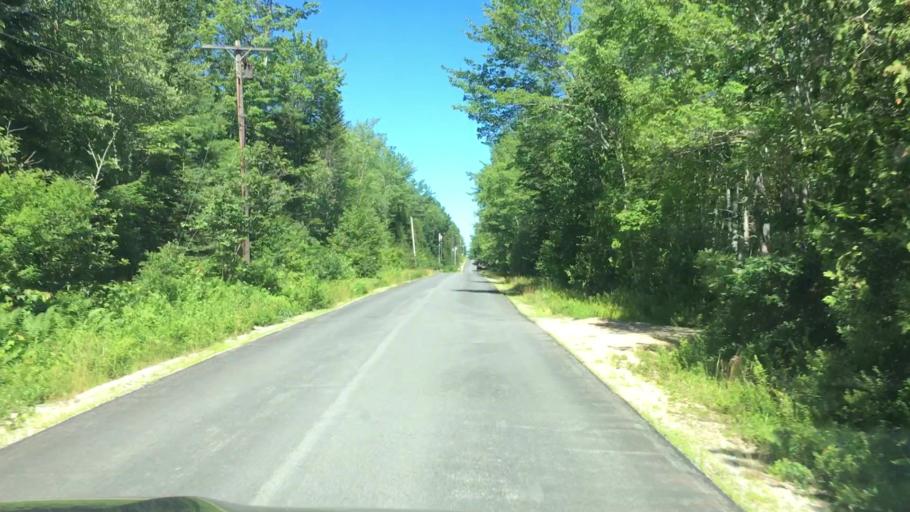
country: US
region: Maine
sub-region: Hancock County
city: Sedgwick
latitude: 44.3167
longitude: -68.6211
